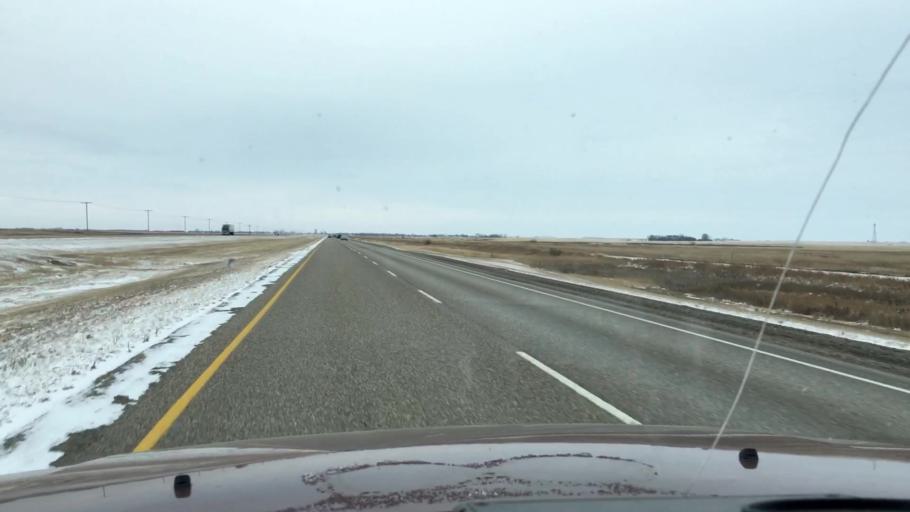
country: CA
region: Saskatchewan
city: Watrous
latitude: 51.0884
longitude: -105.8557
